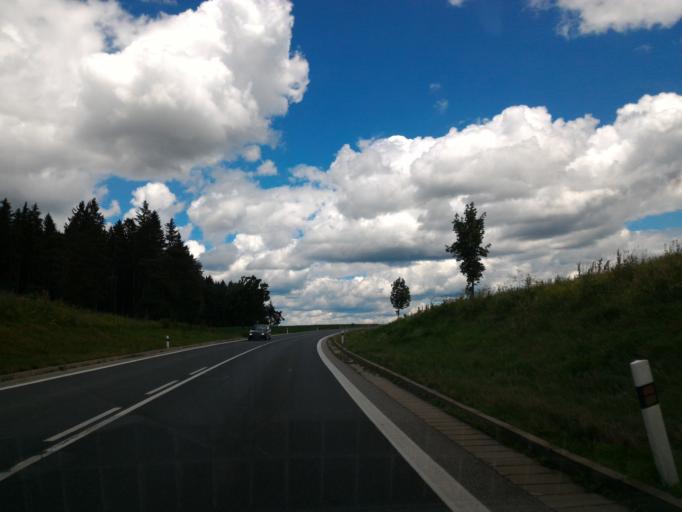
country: CZ
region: Vysocina
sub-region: Okres Zd'ar nad Sazavou
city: Nove Veseli
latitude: 49.5060
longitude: 15.8937
